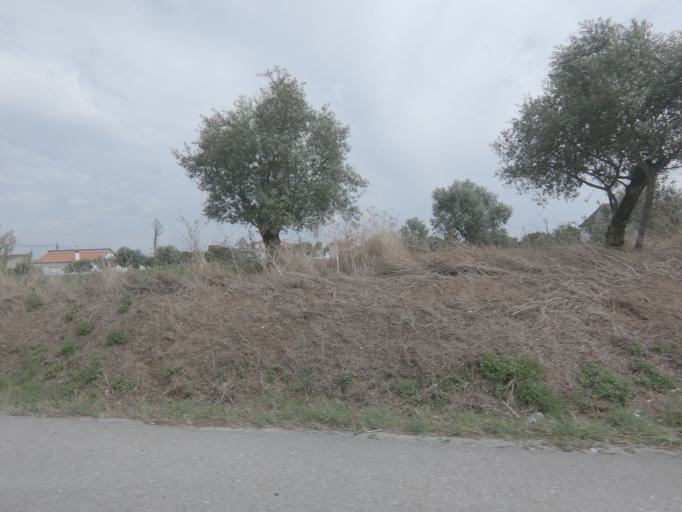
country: PT
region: Leiria
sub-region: Pombal
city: Pombal
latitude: 39.8731
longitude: -8.6888
